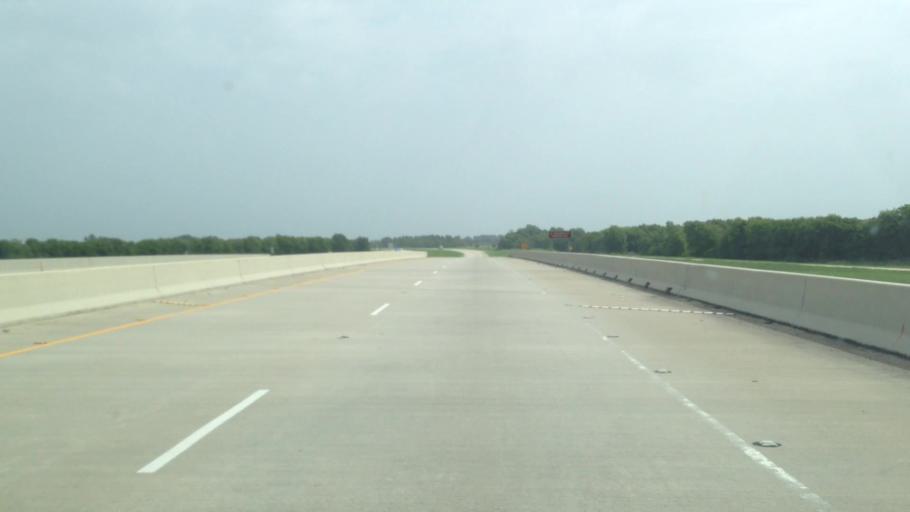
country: US
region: Louisiana
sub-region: Caddo Parish
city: Vivian
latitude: 32.8516
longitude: -93.8644
